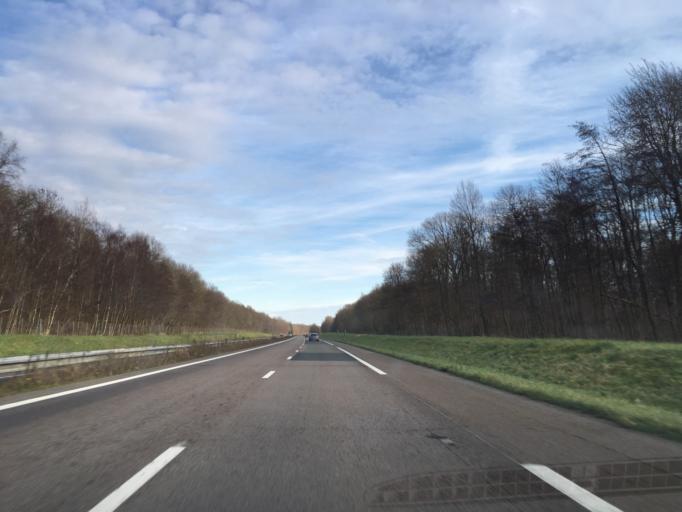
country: FR
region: Picardie
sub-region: Departement de l'Aisne
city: Crezancy
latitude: 49.1154
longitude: 3.5058
